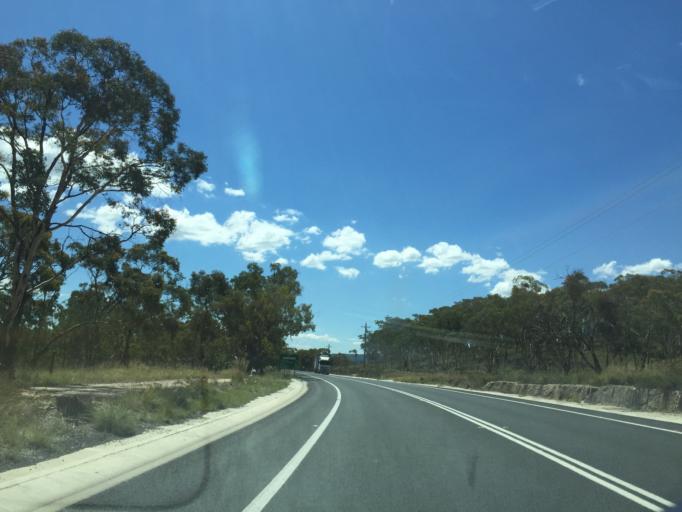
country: AU
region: New South Wales
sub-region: Lithgow
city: Lithgow
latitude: -33.4232
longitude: 150.1039
